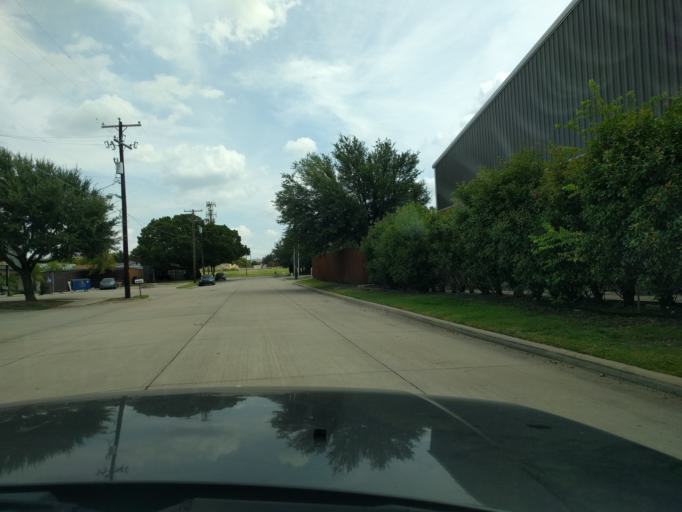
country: US
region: Texas
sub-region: Denton County
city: The Colony
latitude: 33.0259
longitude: -96.8611
